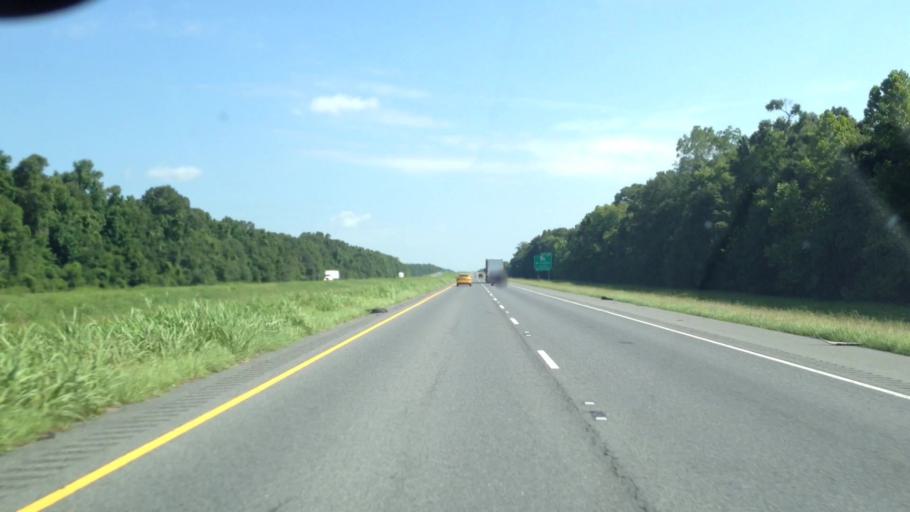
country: US
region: Louisiana
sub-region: Avoyelles Parish
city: Bunkie
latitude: 30.8508
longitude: -92.2284
